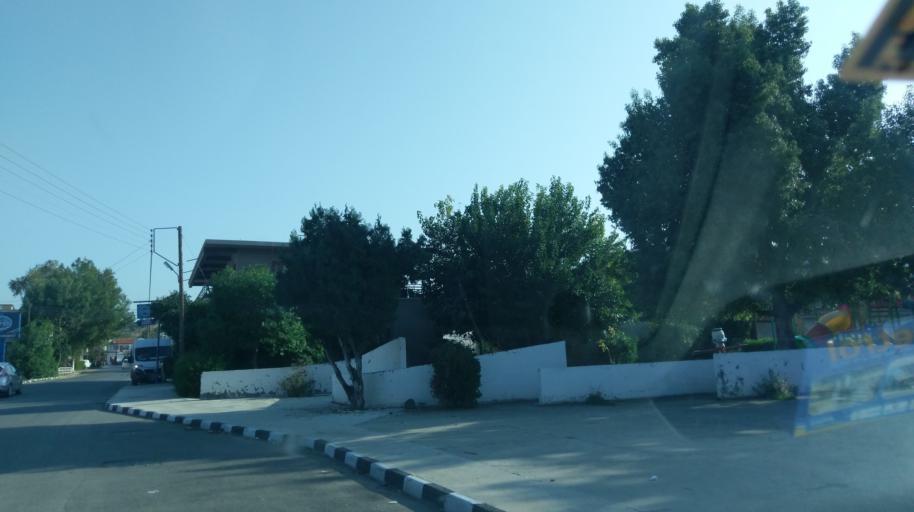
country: CY
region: Lefkosia
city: Lefka
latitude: 35.1444
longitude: 32.8071
